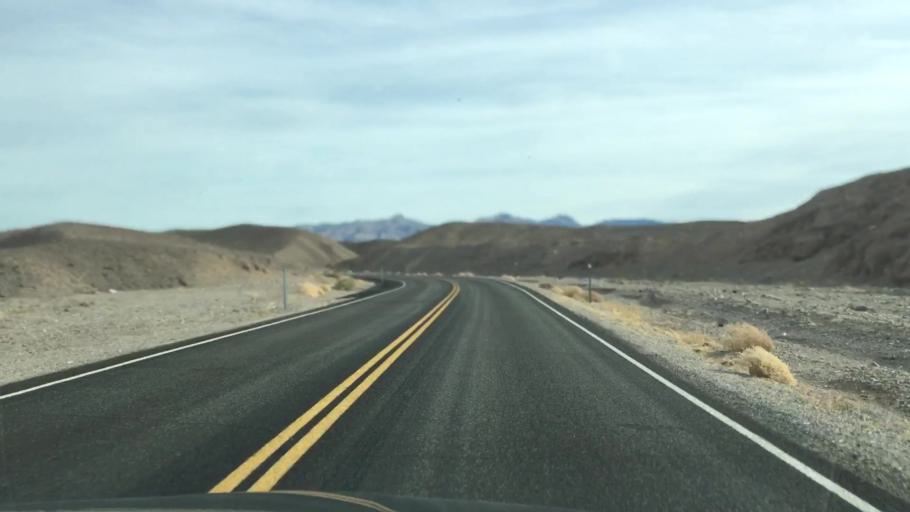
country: US
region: Nevada
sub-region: Nye County
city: Beatty
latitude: 36.6558
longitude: -117.0233
